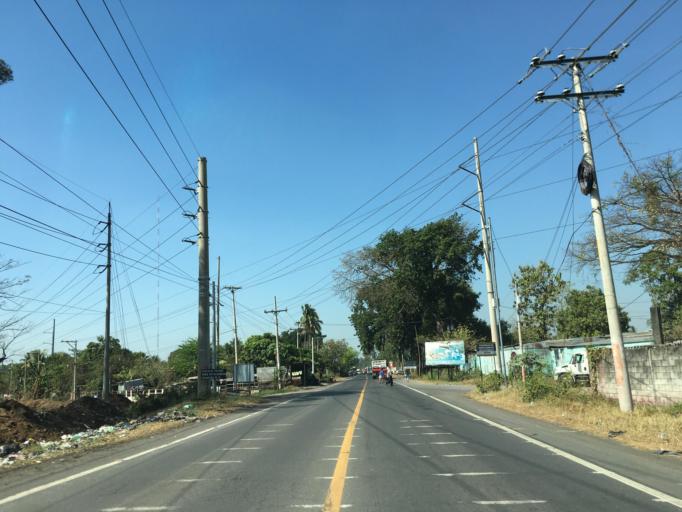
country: GT
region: Escuintla
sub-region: Municipio de Masagua
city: Masagua
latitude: 14.2020
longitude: -90.8447
